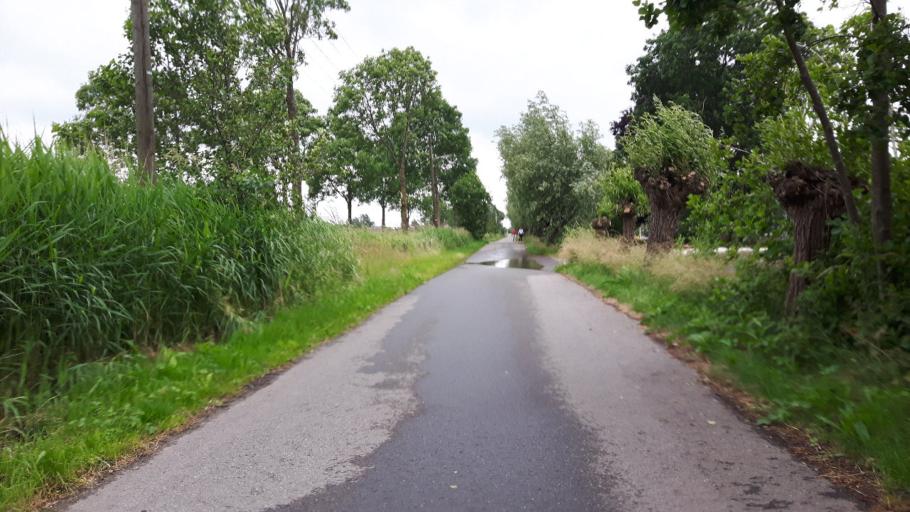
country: NL
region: Utrecht
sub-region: Gemeente Oudewater
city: Oudewater
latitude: 52.0524
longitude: 4.8477
